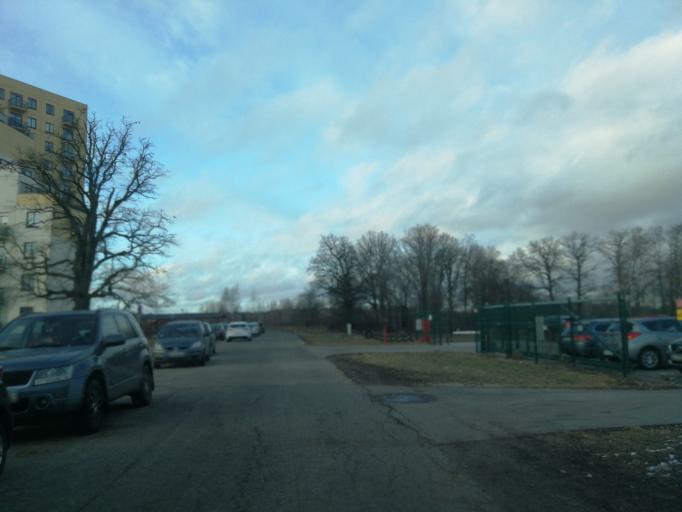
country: LV
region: Adazi
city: Adazi
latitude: 57.0710
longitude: 24.3590
